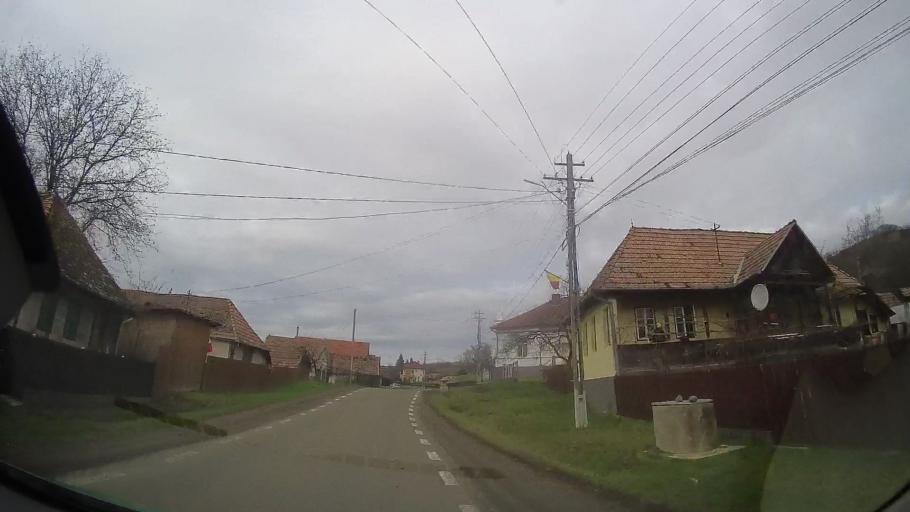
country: RO
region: Mures
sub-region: Comuna Cozma
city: Cozma
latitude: 46.8072
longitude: 24.5237
